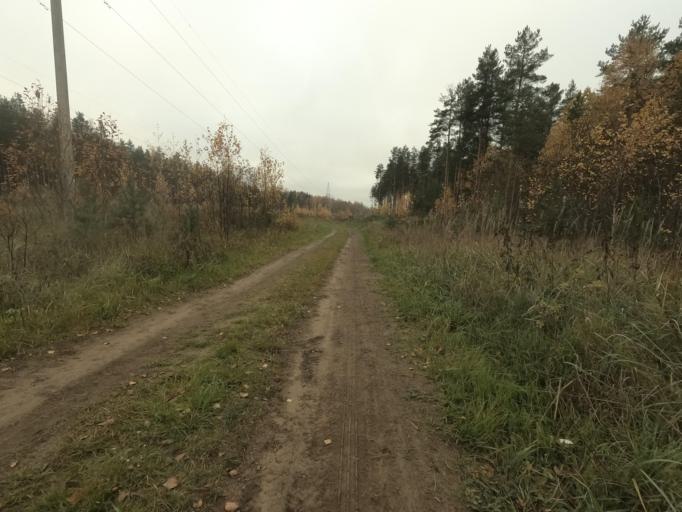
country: RU
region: Leningrad
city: Kirovsk
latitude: 59.8499
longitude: 30.9831
